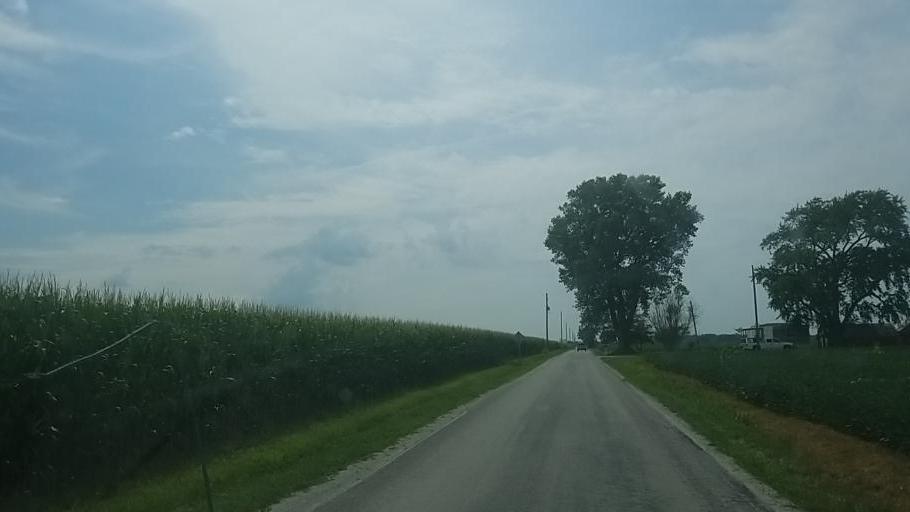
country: US
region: Ohio
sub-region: Hardin County
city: Forest
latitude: 40.7600
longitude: -83.5404
